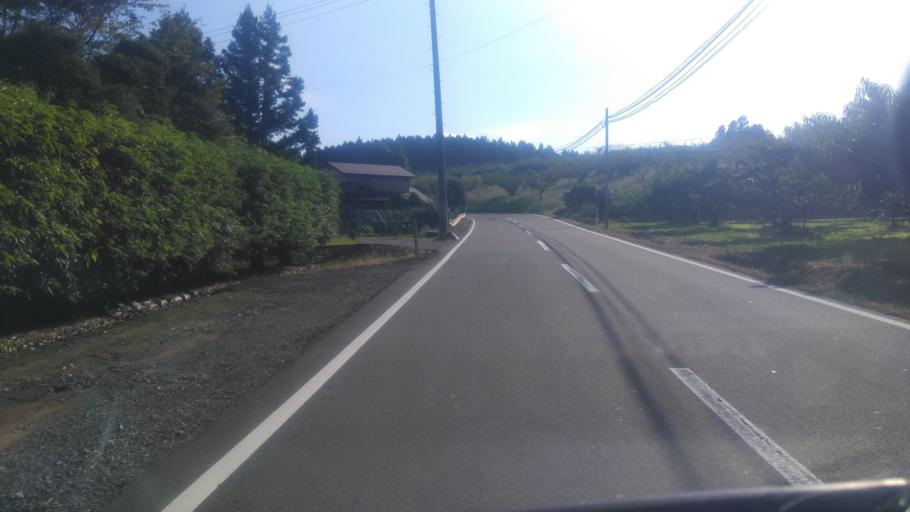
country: JP
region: Miyagi
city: Okawara
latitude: 38.0952
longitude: 140.6704
